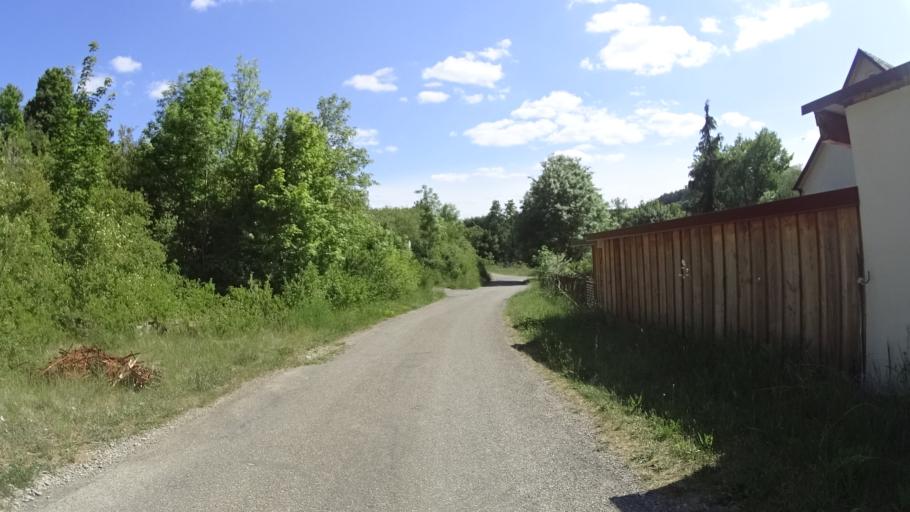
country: DE
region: Baden-Wuerttemberg
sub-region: Karlsruhe Region
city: Hardheim
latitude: 49.5851
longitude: 9.4857
